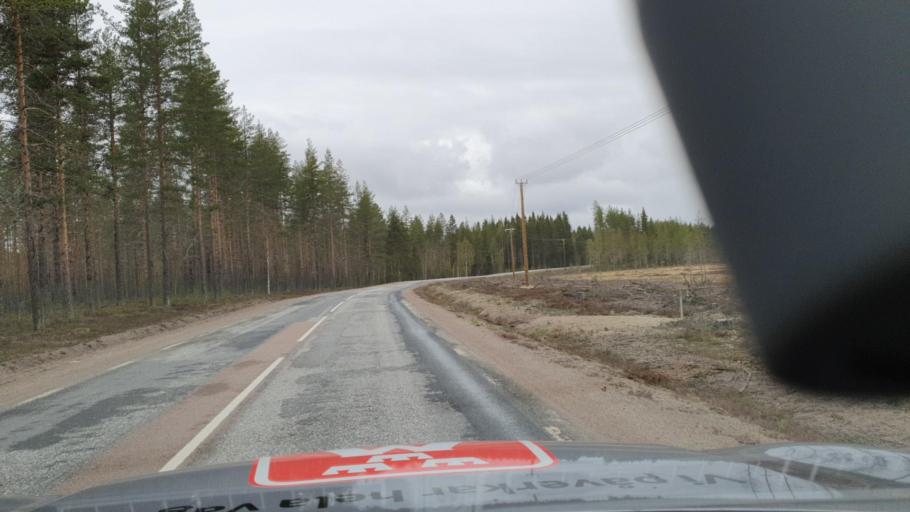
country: SE
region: Vaesternorrland
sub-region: Solleftea Kommun
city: Solleftea
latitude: 63.6342
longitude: 17.4258
